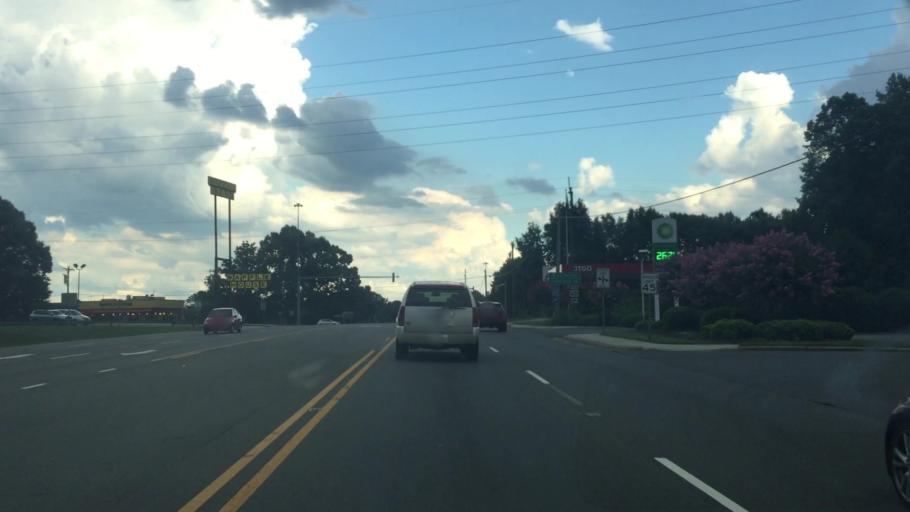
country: US
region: North Carolina
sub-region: Rowan County
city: Salisbury
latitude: 35.6436
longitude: -80.4835
